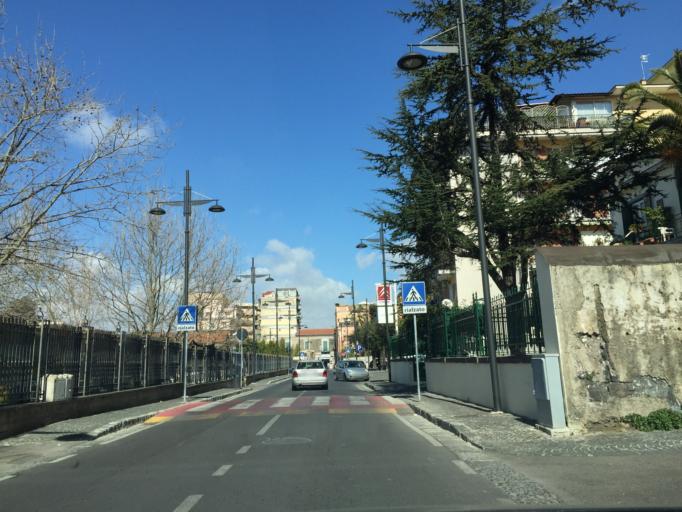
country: IT
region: Campania
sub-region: Provincia di Napoli
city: San Giorgio a Cremano
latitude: 40.8266
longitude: 14.3404
